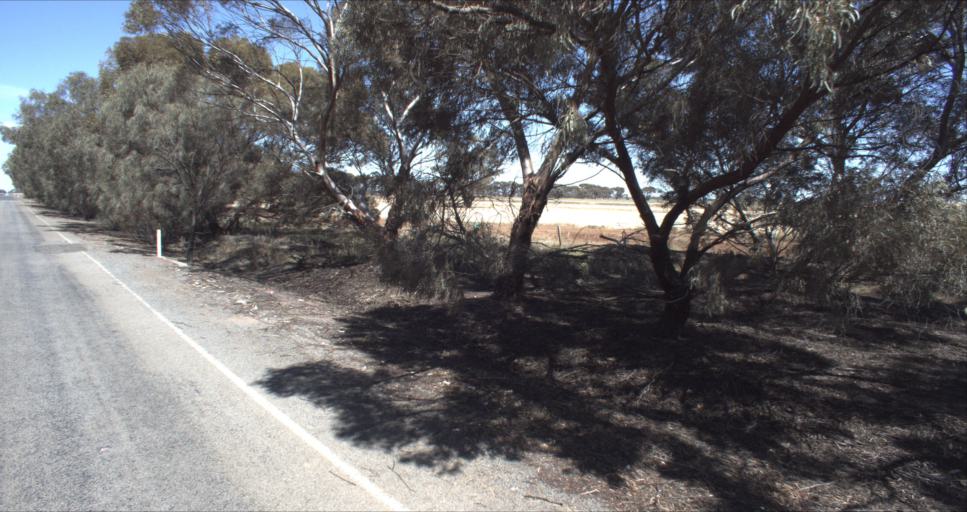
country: AU
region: New South Wales
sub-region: Leeton
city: Leeton
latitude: -34.4703
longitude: 146.2925
